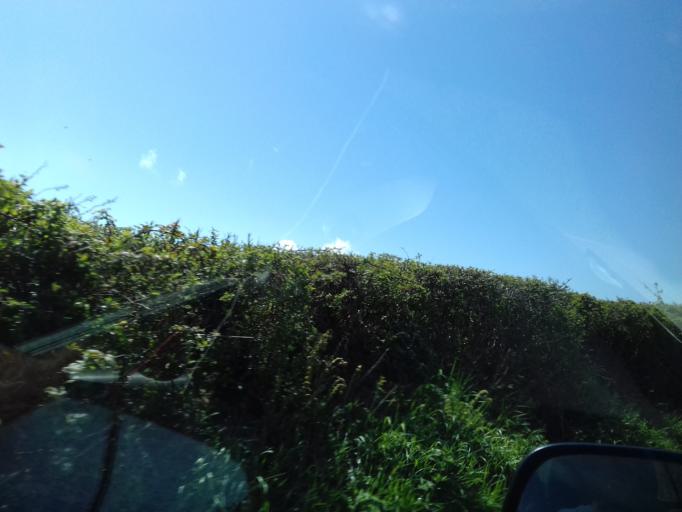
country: IE
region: Munster
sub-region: Waterford
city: Dunmore East
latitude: 52.2027
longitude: -6.8567
